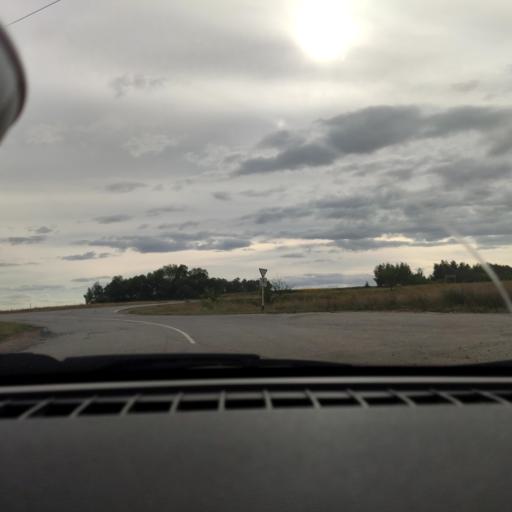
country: RU
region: Samara
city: Georgiyevka
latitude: 53.4822
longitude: 50.9380
